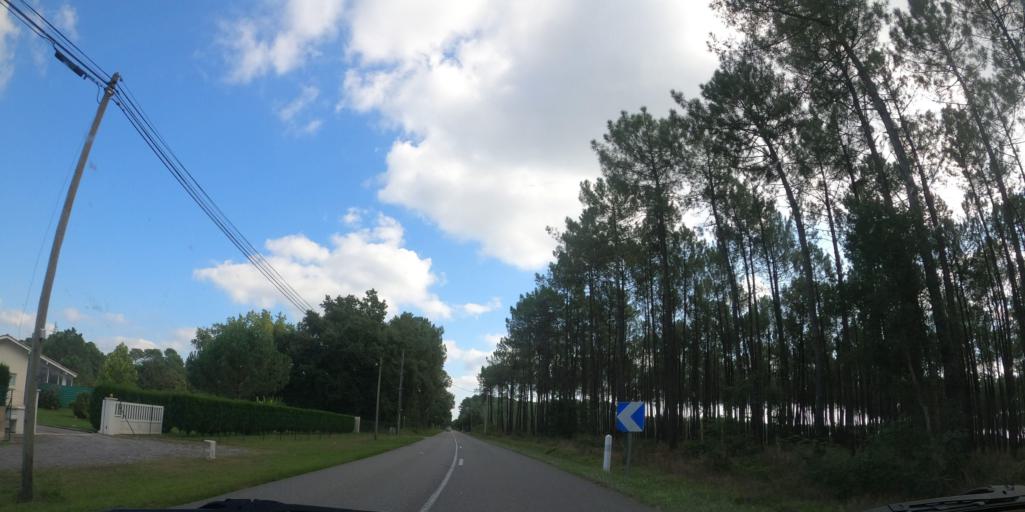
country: FR
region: Aquitaine
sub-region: Departement des Landes
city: Soustons
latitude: 43.7372
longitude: -1.2949
